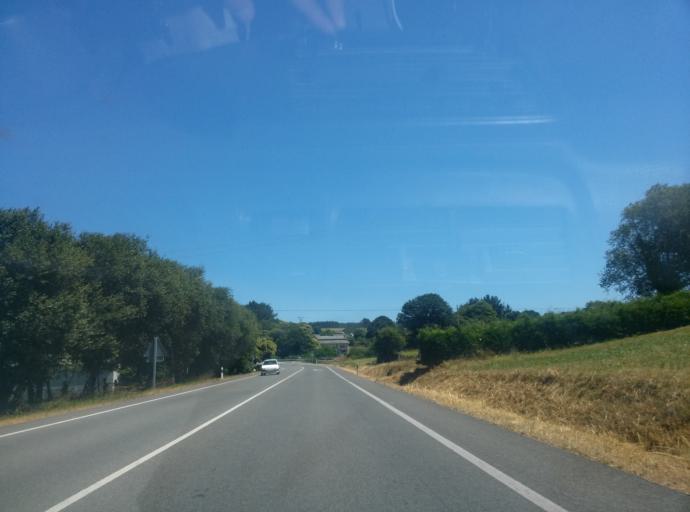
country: ES
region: Galicia
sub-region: Provincia de Lugo
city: Castro de Rei
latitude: 43.2318
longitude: -7.3767
